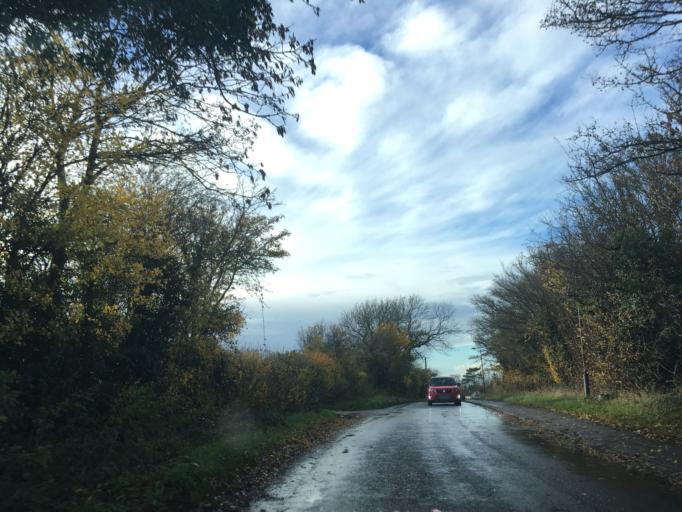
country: GB
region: England
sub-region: South Gloucestershire
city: Pucklechurch
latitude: 51.4904
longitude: -2.4441
